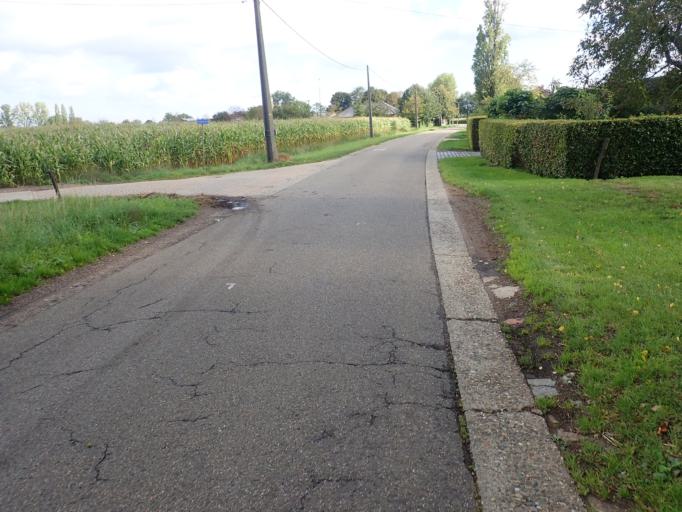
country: BE
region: Flanders
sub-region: Provincie Antwerpen
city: Herenthout
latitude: 51.1437
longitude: 4.7993
